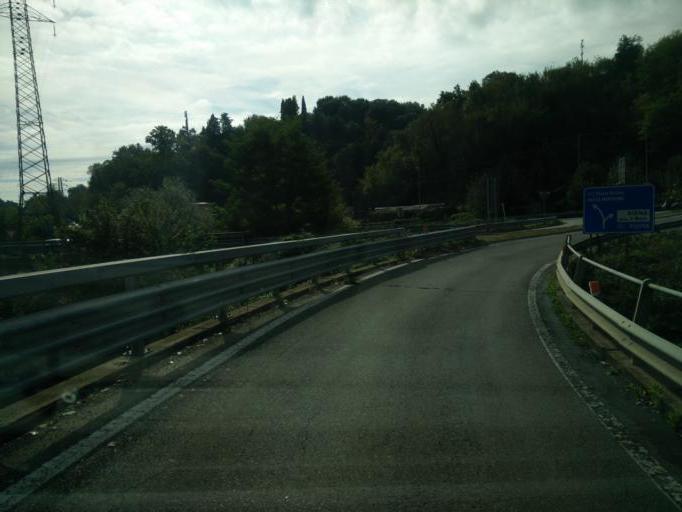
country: IT
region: Tuscany
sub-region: Provincia di Siena
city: Siena
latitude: 43.3076
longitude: 11.3145
